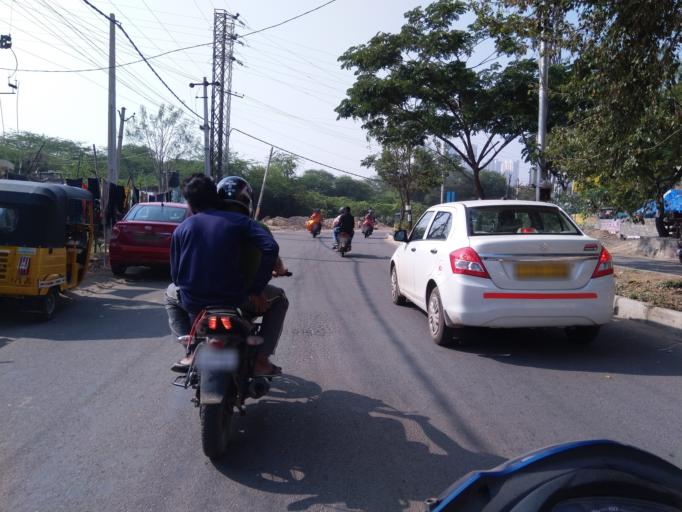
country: IN
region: Telangana
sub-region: Rangareddi
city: Kukatpalli
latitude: 17.4847
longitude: 78.3990
